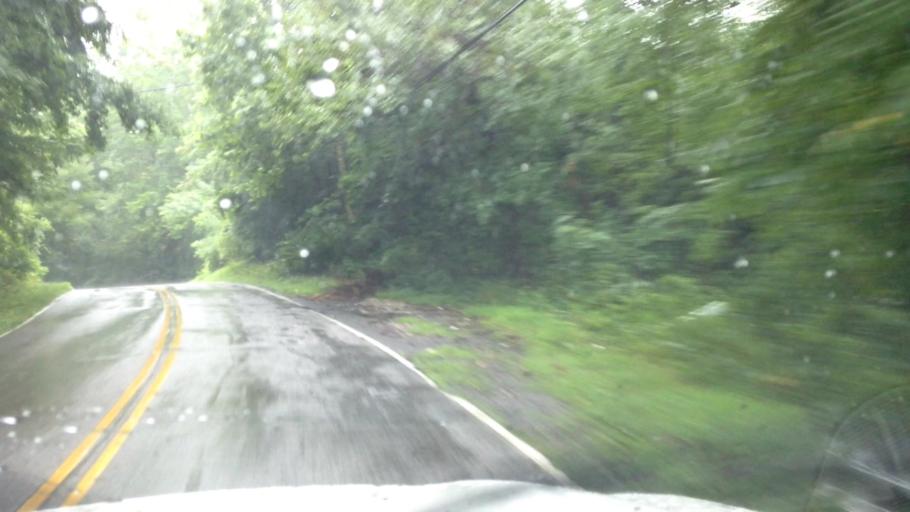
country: US
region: Maryland
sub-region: Anne Arundel County
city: Odenton
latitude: 39.1028
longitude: -76.6907
